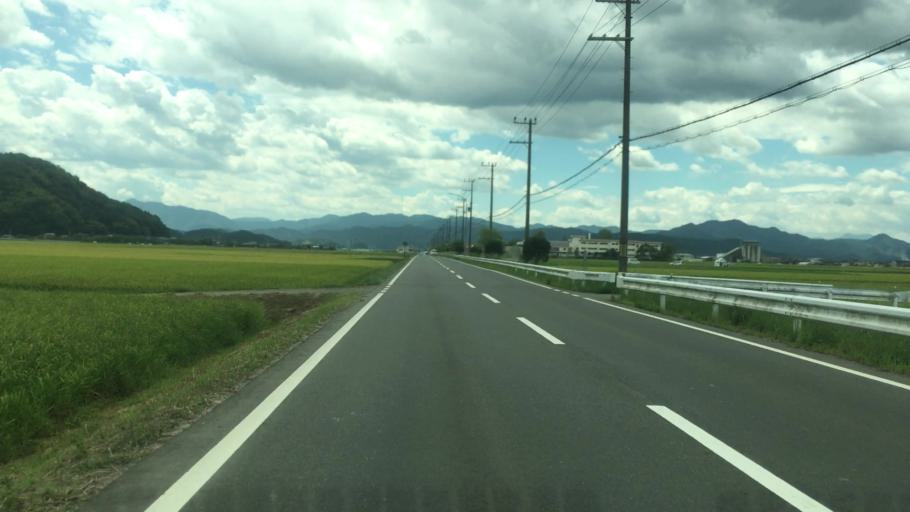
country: JP
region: Hyogo
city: Toyooka
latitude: 35.5363
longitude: 134.8397
